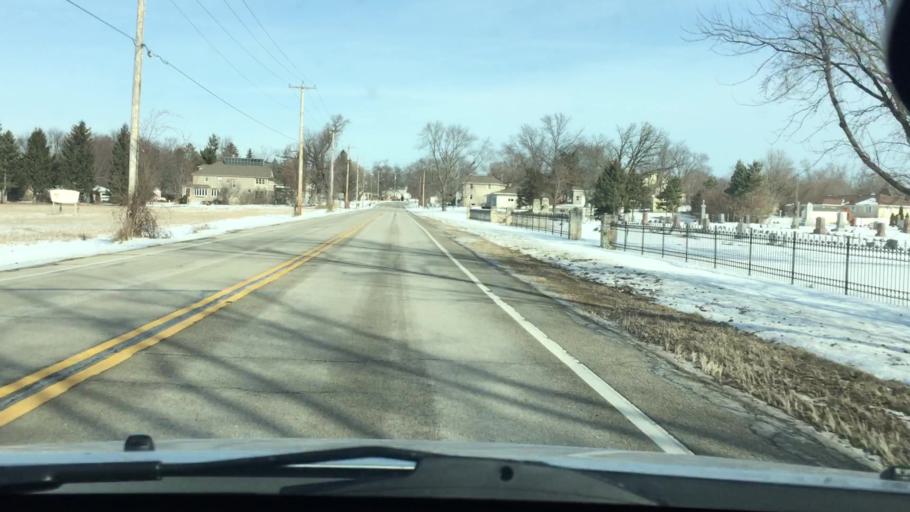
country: US
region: Wisconsin
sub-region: Waukesha County
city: Eagle
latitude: 42.8742
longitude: -88.4811
